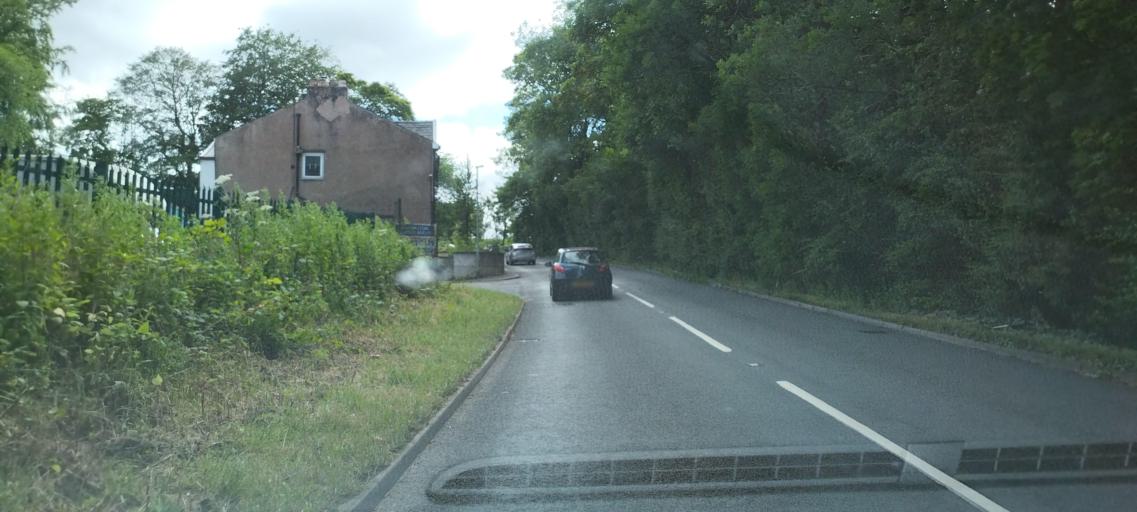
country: GB
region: England
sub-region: Blackburn with Darwen
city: Blackburn
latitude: 53.7195
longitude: -2.5587
